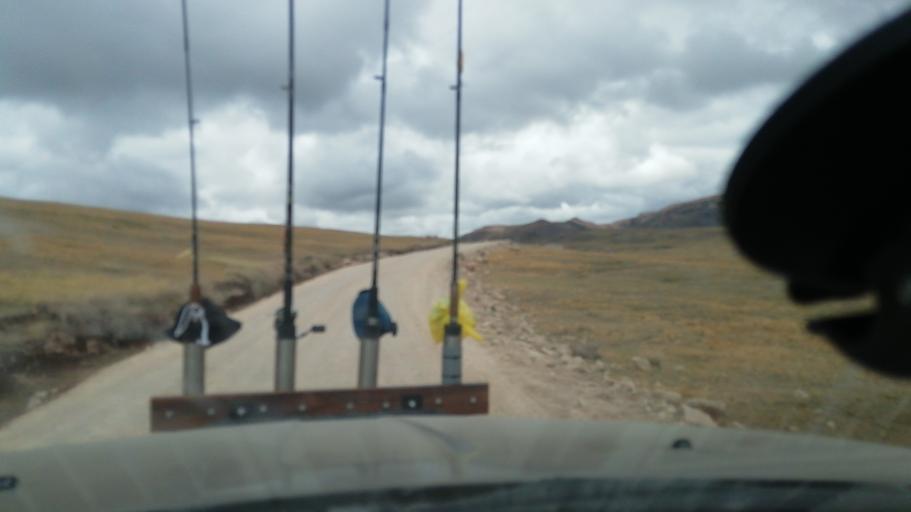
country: PE
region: Huancavelica
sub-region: Provincia de Huancavelica
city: Acobambilla
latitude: -12.5368
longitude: -75.5546
